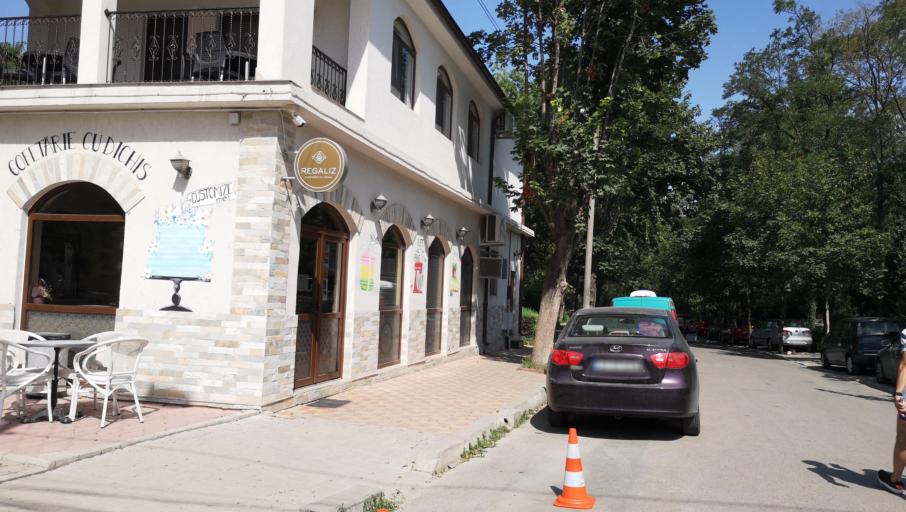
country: RO
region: Constanta
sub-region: Oras Eforie
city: Eforie Nord
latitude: 44.0668
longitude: 28.6352
